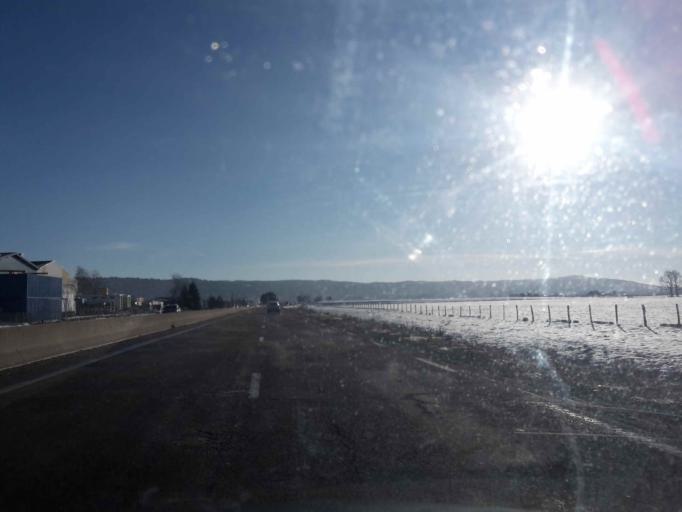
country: FR
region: Franche-Comte
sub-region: Departement du Doubs
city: Doubs
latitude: 46.9162
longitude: 6.3346
